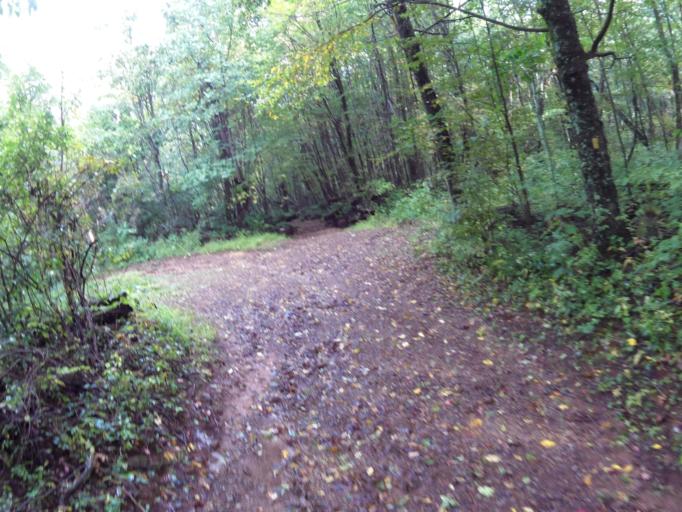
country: US
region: Virginia
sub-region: Rappahannock County
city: Washington
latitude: 38.7744
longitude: -78.2925
